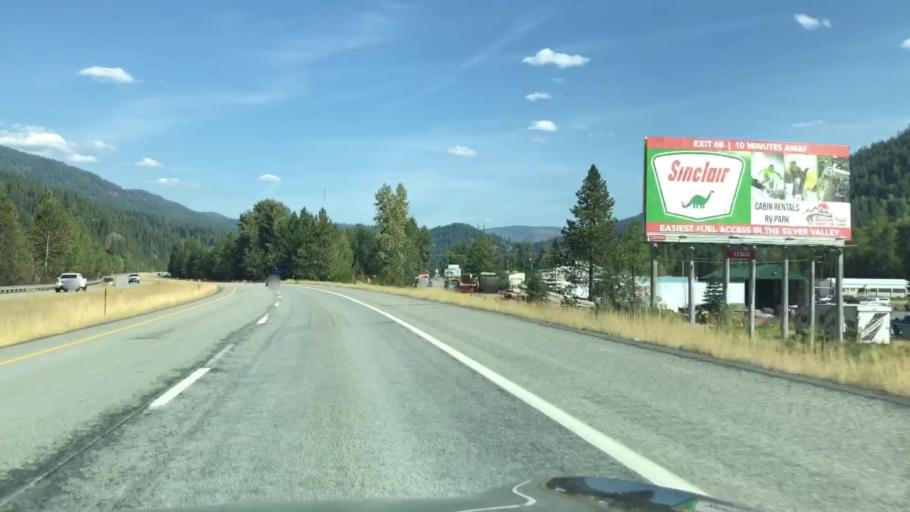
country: US
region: Idaho
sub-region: Shoshone County
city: Osburn
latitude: 47.5094
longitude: -116.0144
